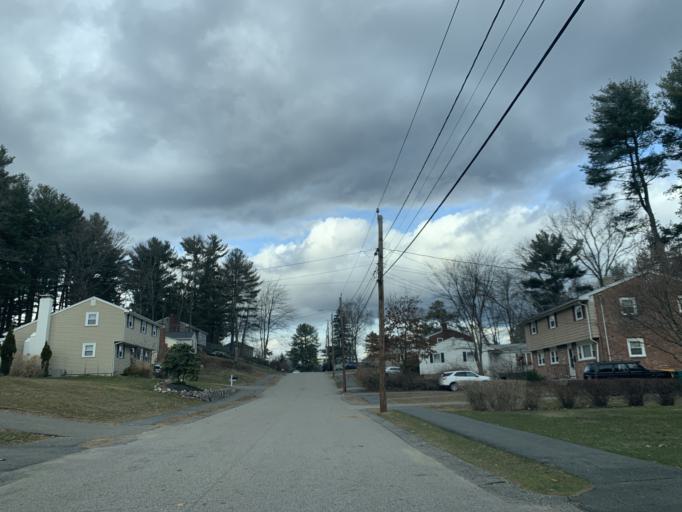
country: US
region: Massachusetts
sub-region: Norfolk County
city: Norwood
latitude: 42.1783
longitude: -71.1747
